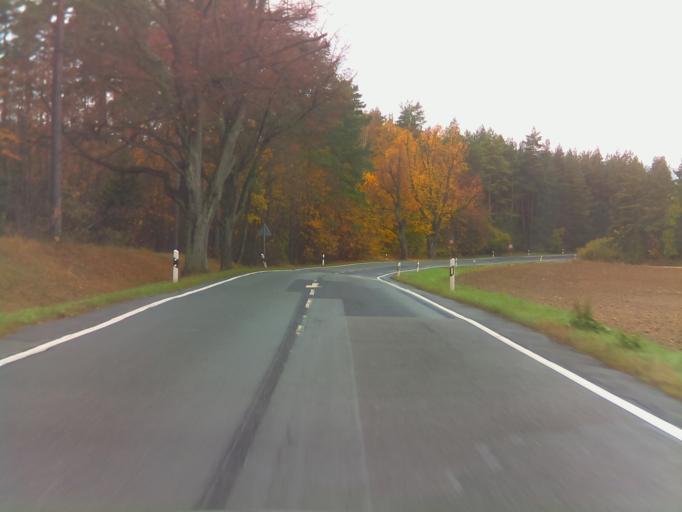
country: DE
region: Thuringia
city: Stadtilm
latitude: 50.7679
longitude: 11.1025
